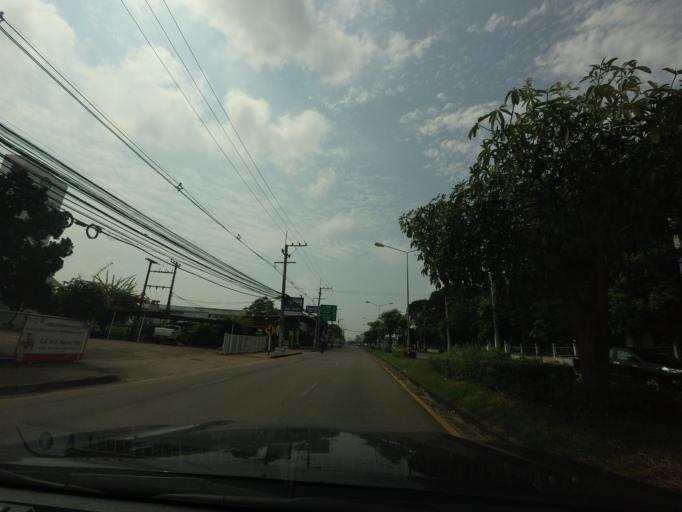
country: TH
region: Phrae
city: Phrae
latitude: 18.1278
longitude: 100.1433
